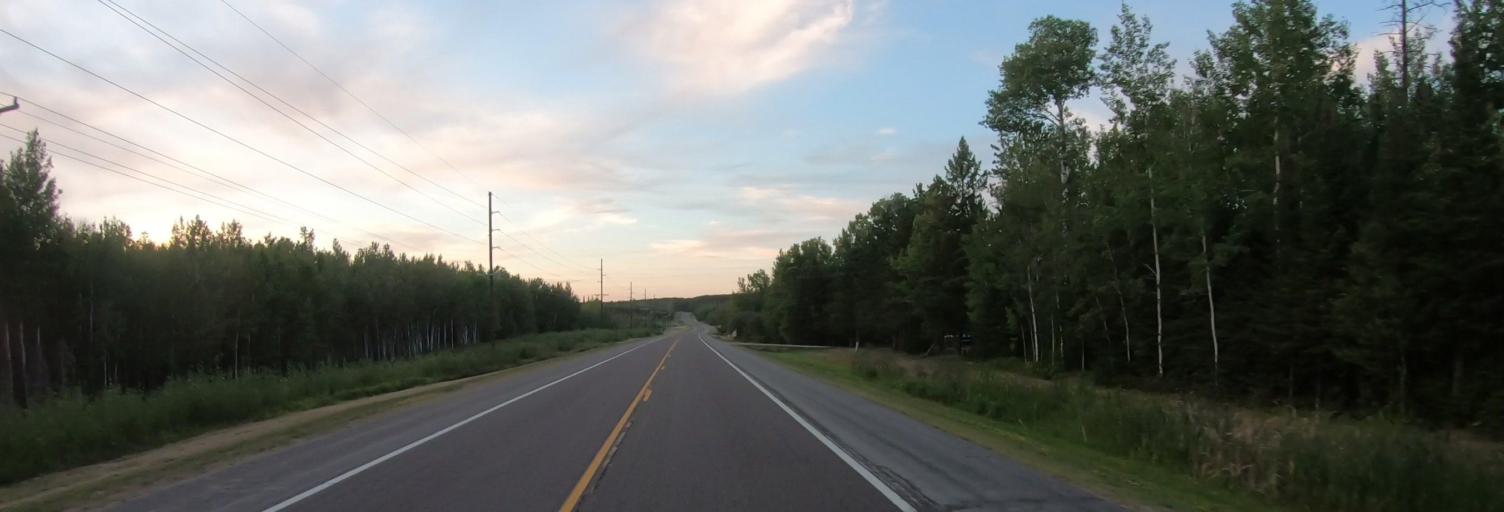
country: US
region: Minnesota
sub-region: Saint Louis County
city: Aurora
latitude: 47.8269
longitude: -92.3728
